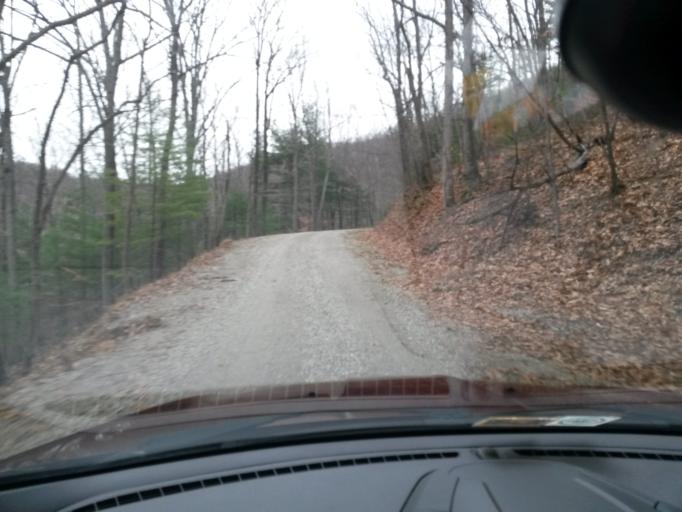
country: US
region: Virginia
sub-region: City of Buena Vista
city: Buena Vista
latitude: 37.7140
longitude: -79.2414
